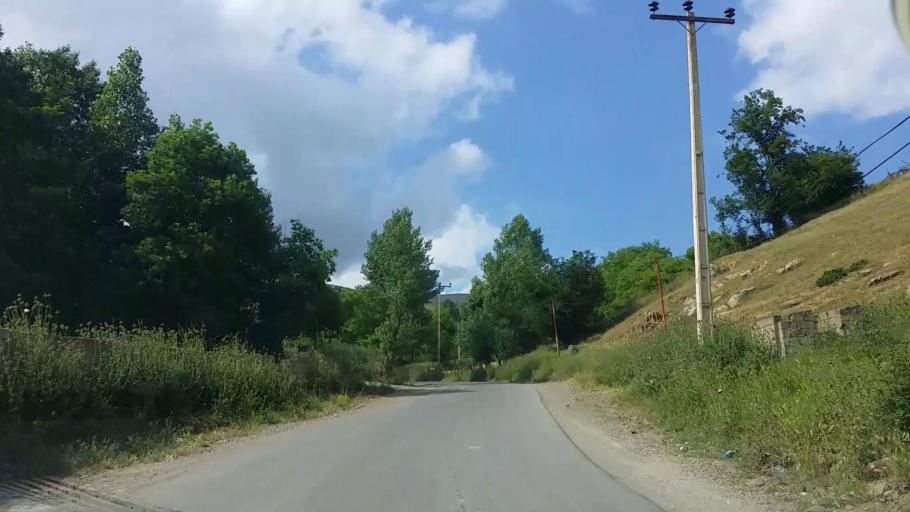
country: IR
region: Mazandaran
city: Chalus
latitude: 36.5177
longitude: 51.2597
